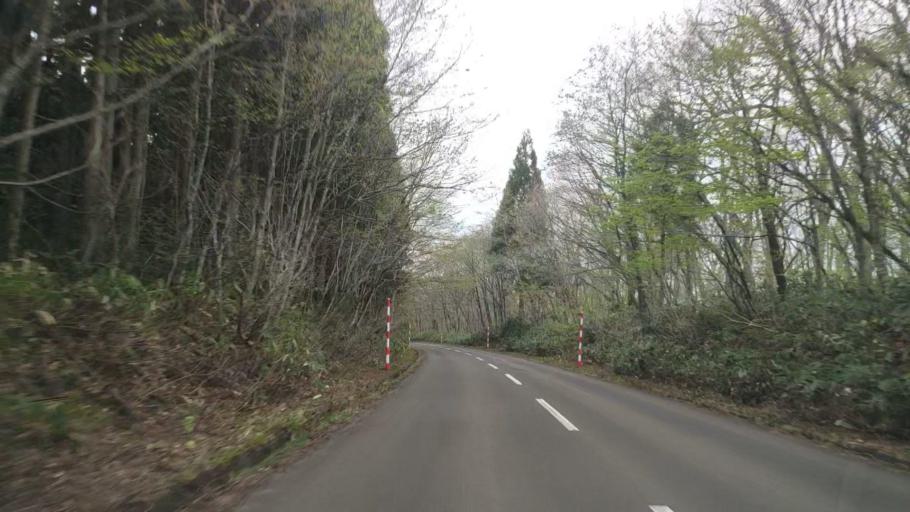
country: JP
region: Akita
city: Hanawa
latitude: 40.3891
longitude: 140.7941
